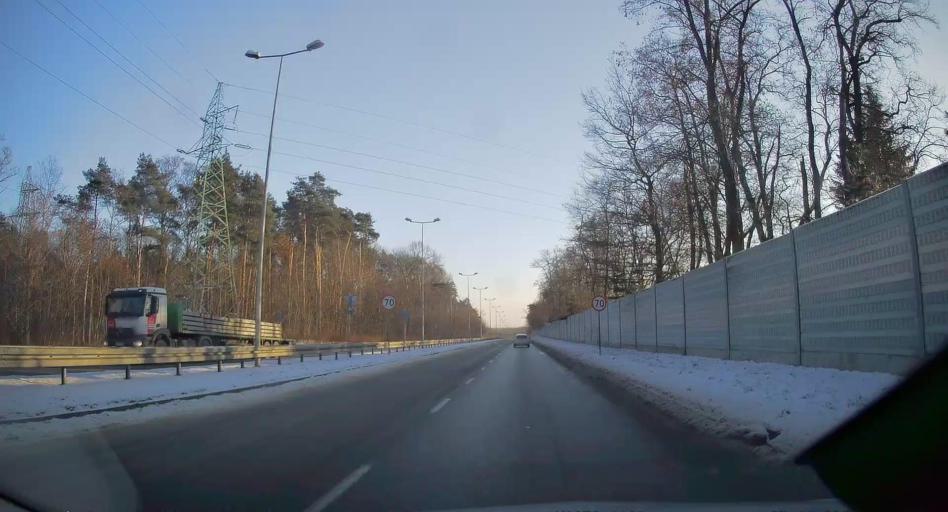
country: PL
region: Lodz Voivodeship
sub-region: Piotrkow Trybunalski
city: Piotrkow Trybunalski
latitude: 51.4192
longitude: 19.7200
